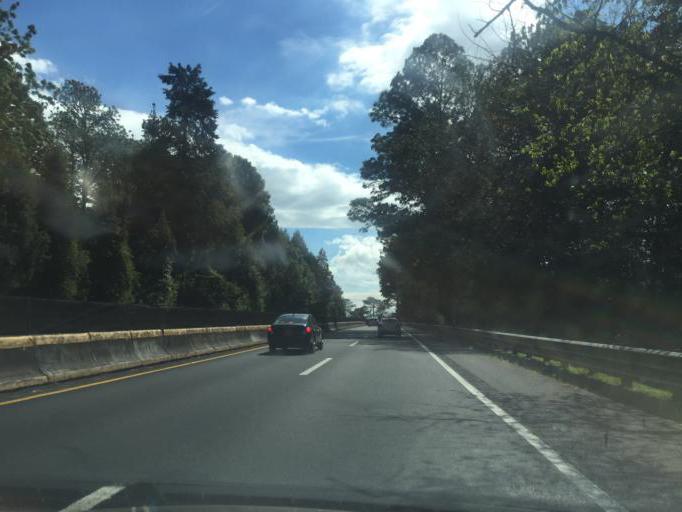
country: MX
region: Morelos
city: Tres Marias
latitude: 19.0318
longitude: -99.2226
